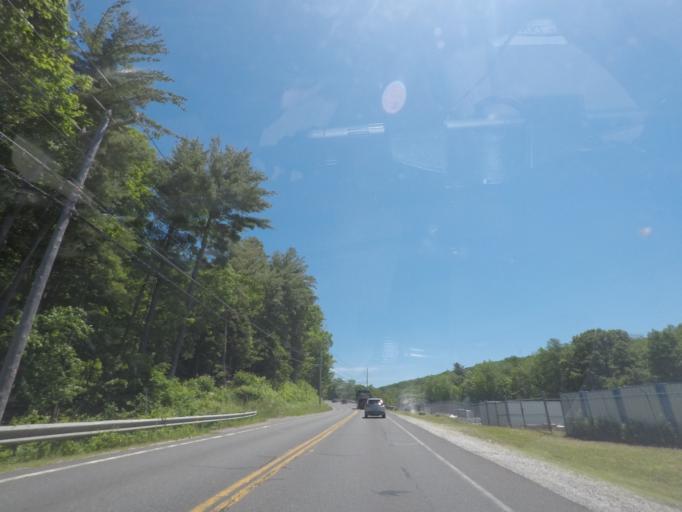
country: US
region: Massachusetts
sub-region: Berkshire County
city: Lee
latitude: 42.2956
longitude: -73.1757
